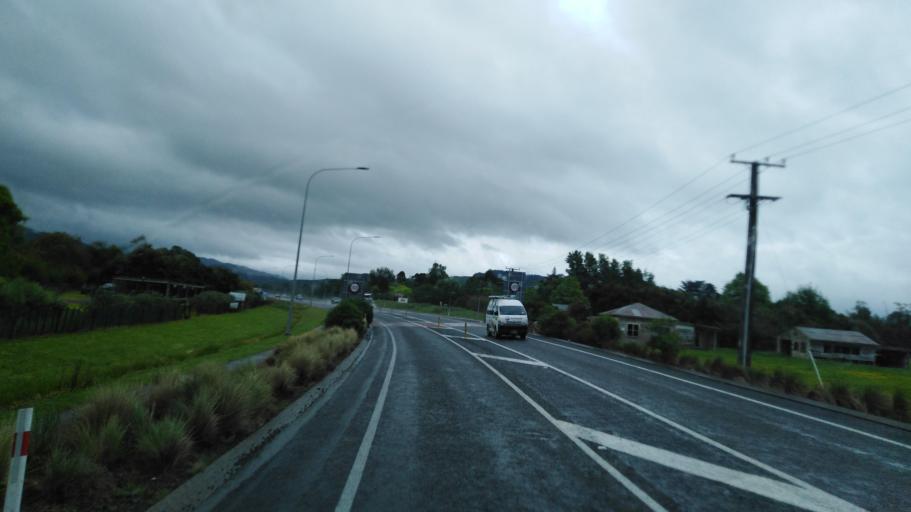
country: NZ
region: Wellington
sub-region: Kapiti Coast District
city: Otaki
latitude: -40.7190
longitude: 175.2139
